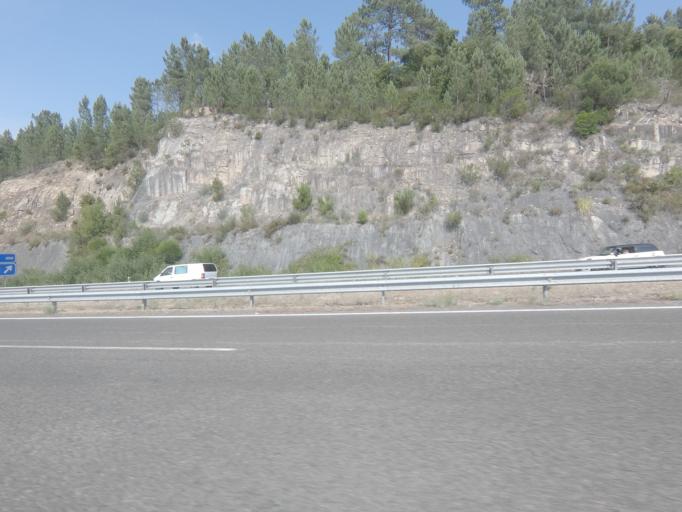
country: ES
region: Galicia
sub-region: Provincia de Ourense
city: Ourense
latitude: 42.2942
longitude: -7.8777
